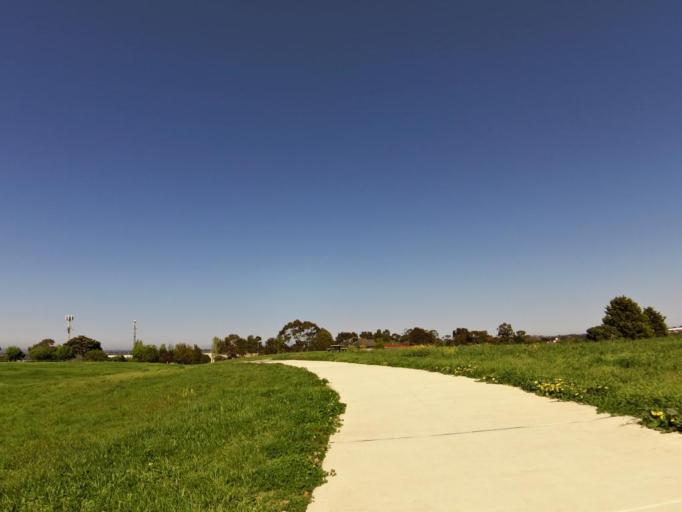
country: AU
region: Victoria
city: Plenty
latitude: -37.6853
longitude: 145.1145
